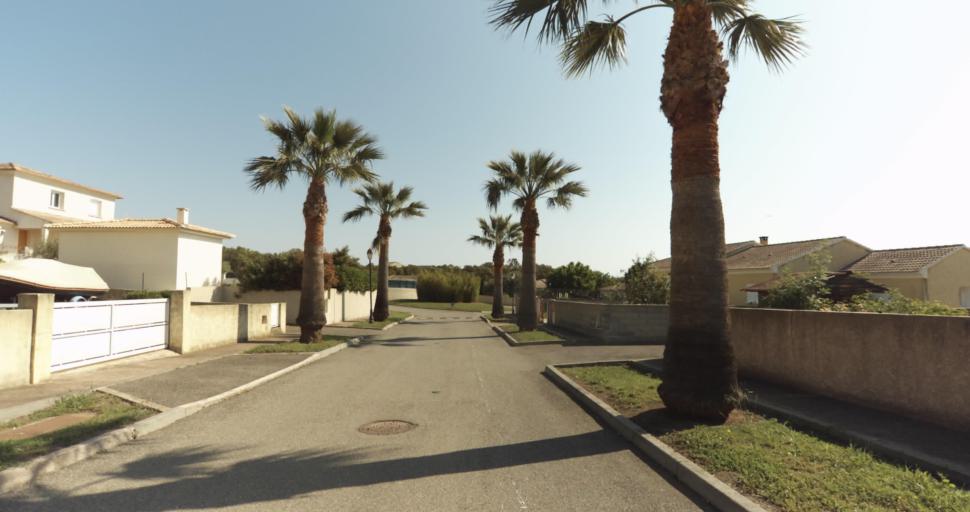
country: FR
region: Corsica
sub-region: Departement de la Haute-Corse
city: Biguglia
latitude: 42.6213
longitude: 9.4322
